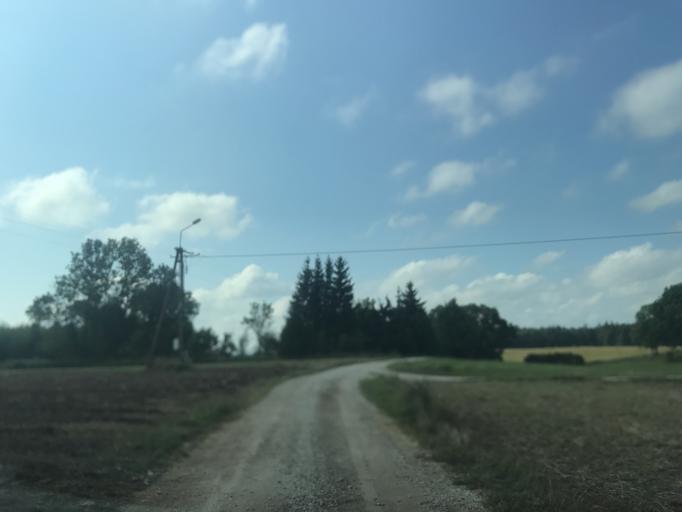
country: PL
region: Kujawsko-Pomorskie
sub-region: Powiat brodnicki
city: Brodnica
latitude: 53.3468
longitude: 19.4689
